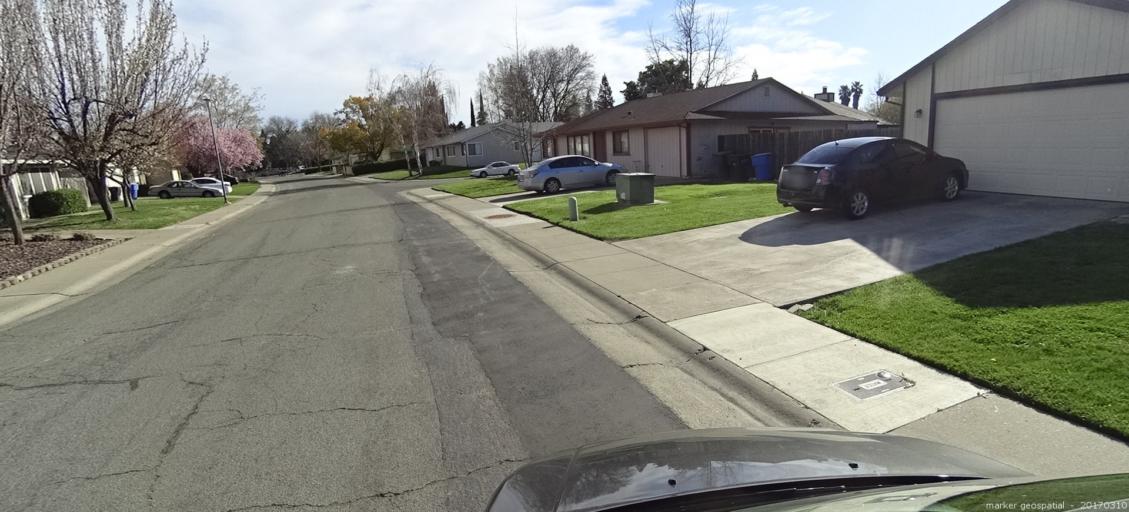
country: US
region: California
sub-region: Sacramento County
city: Parkway
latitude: 38.4898
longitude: -121.5380
